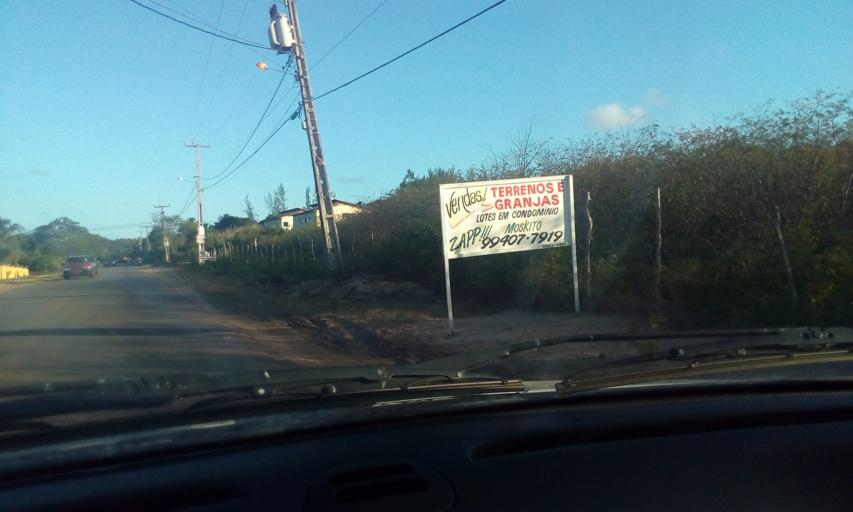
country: BR
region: Rio Grande do Norte
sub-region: Parnamirim
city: Parnamirim
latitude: -5.9553
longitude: -35.1713
